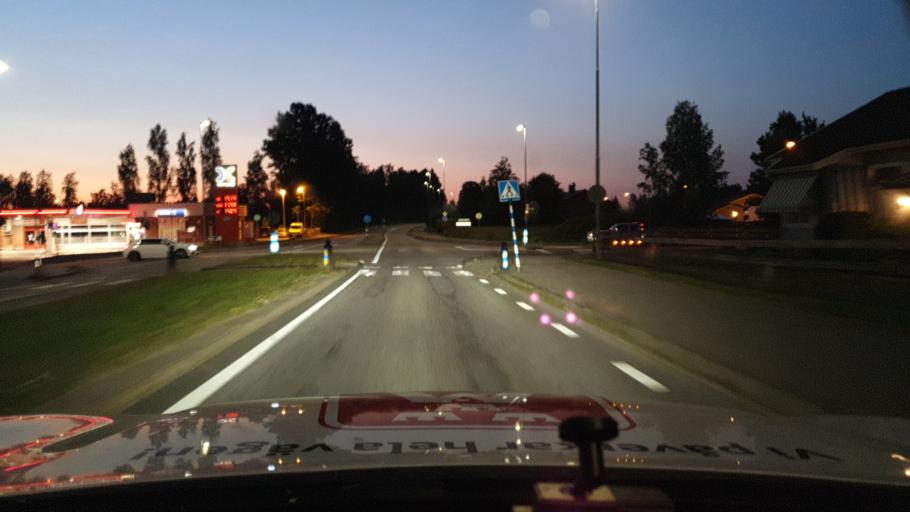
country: SE
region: OErebro
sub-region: Degerfors Kommun
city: Degerfors
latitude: 59.2479
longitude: 14.4372
